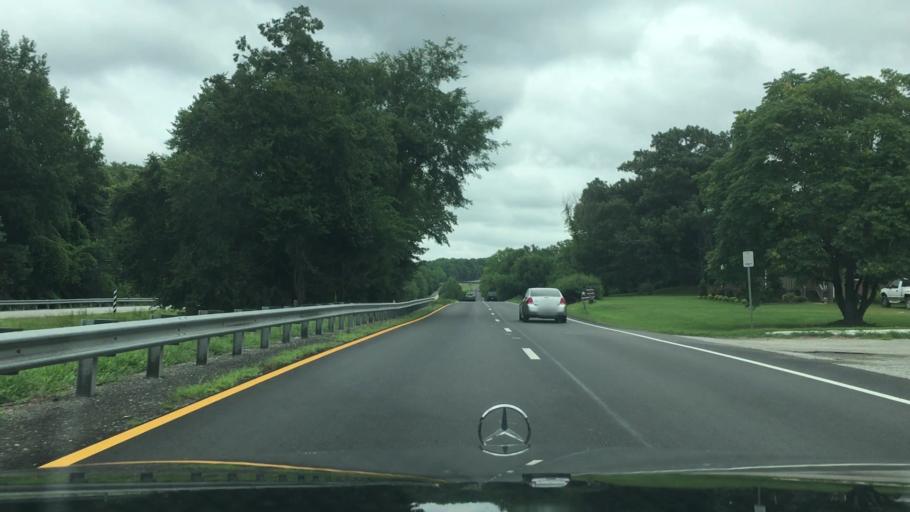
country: US
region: Virginia
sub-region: Prince Edward County
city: Farmville
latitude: 37.2738
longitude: -78.3034
